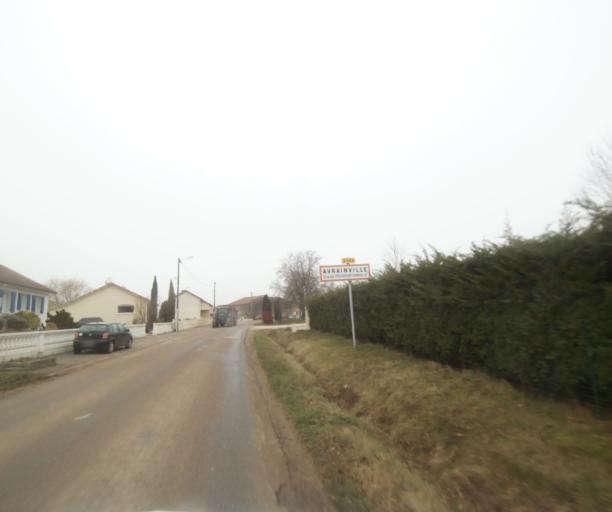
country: FR
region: Champagne-Ardenne
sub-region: Departement de la Haute-Marne
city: Bienville
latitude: 48.5287
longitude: 5.0445
